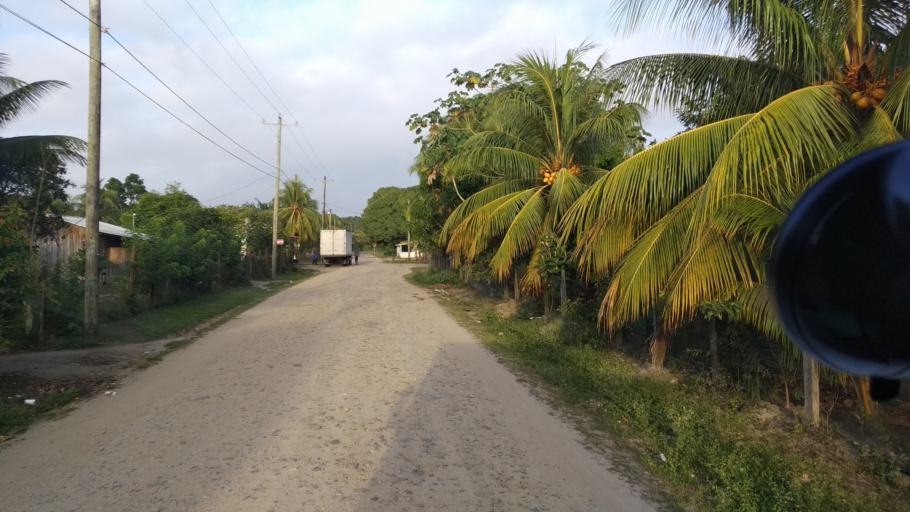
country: BZ
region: Stann Creek
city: Placencia
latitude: 16.5709
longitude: -88.5280
